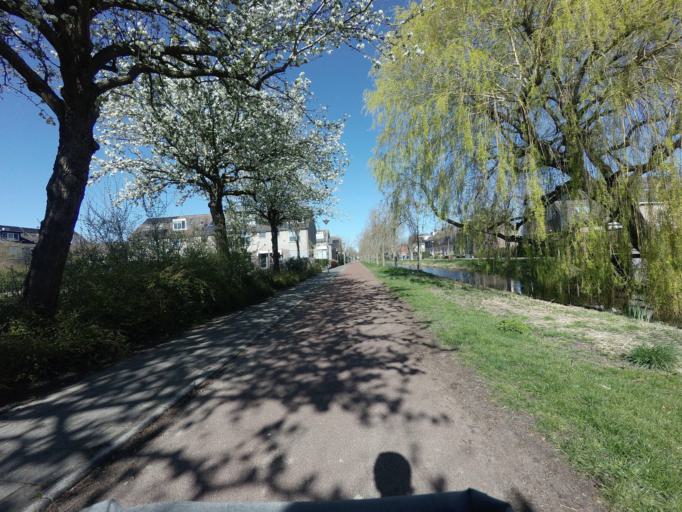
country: NL
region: Utrecht
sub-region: Gemeente Woerden
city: Woerden
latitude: 52.0794
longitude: 4.8574
